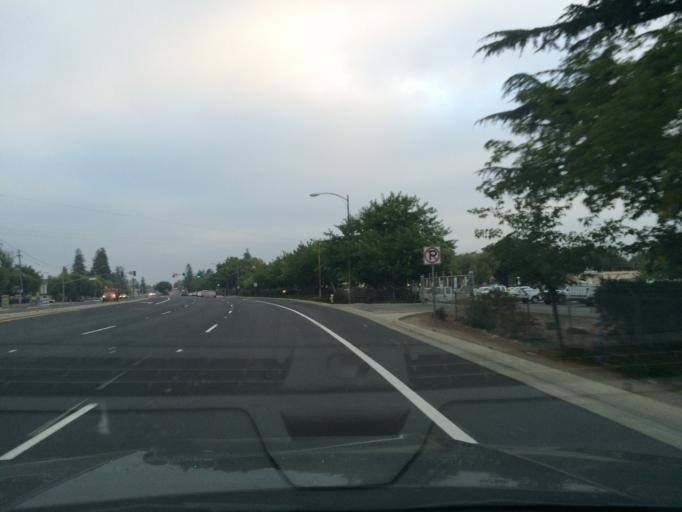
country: US
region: California
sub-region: Santa Clara County
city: Seven Trees
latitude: 37.2442
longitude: -121.8746
